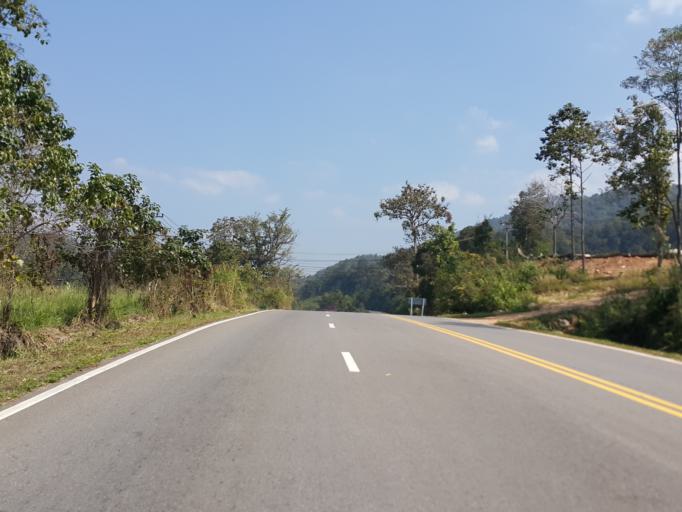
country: TH
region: Chiang Mai
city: Mae On
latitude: 19.0243
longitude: 99.3141
